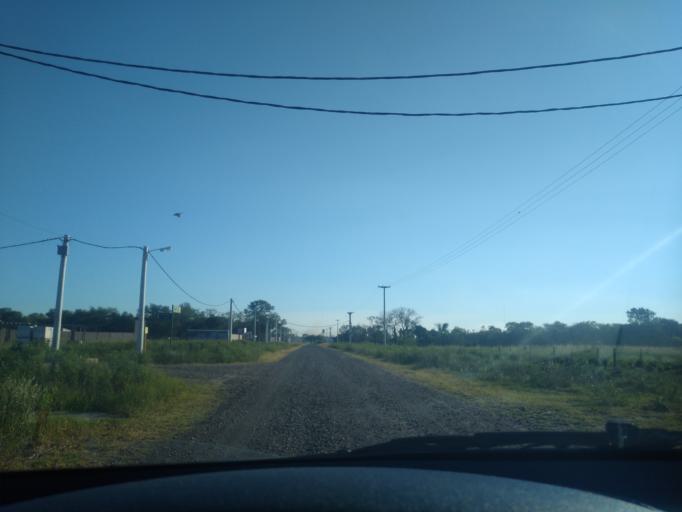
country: AR
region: Chaco
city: Resistencia
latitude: -27.4093
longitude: -58.9540
